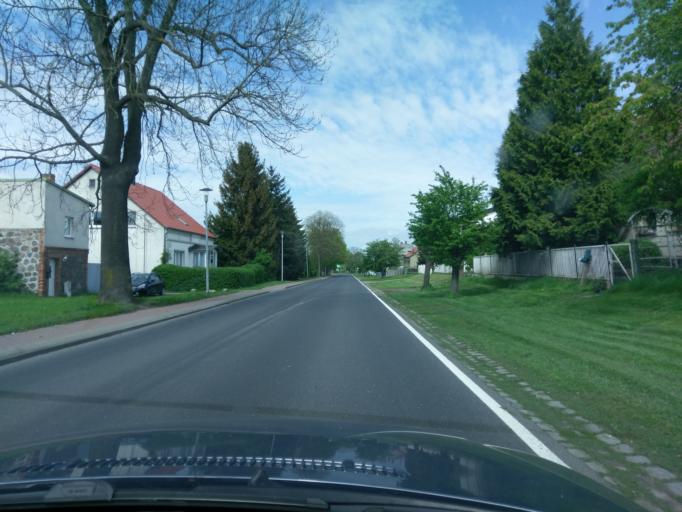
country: DE
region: Brandenburg
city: Werftpfuhl
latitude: 52.7409
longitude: 13.8417
